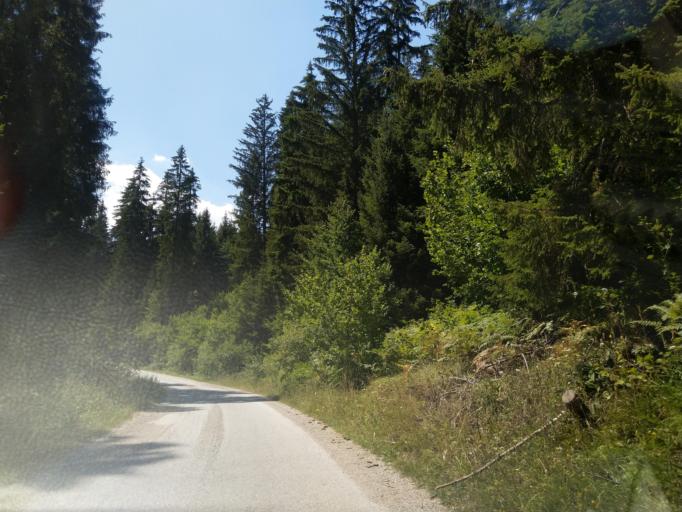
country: RS
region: Central Serbia
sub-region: Zlatiborski Okrug
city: Nova Varos
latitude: 43.4733
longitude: 19.9643
